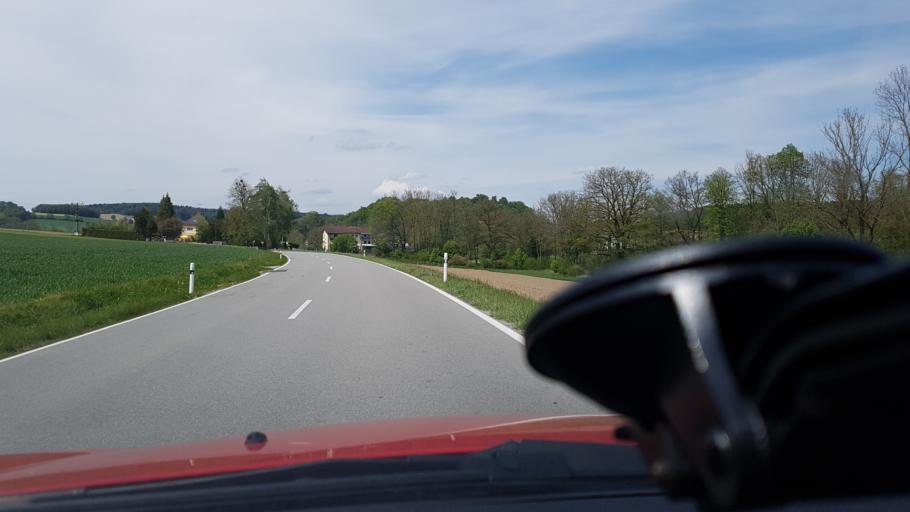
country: DE
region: Bavaria
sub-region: Lower Bavaria
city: Ering
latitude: 48.3179
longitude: 13.1364
